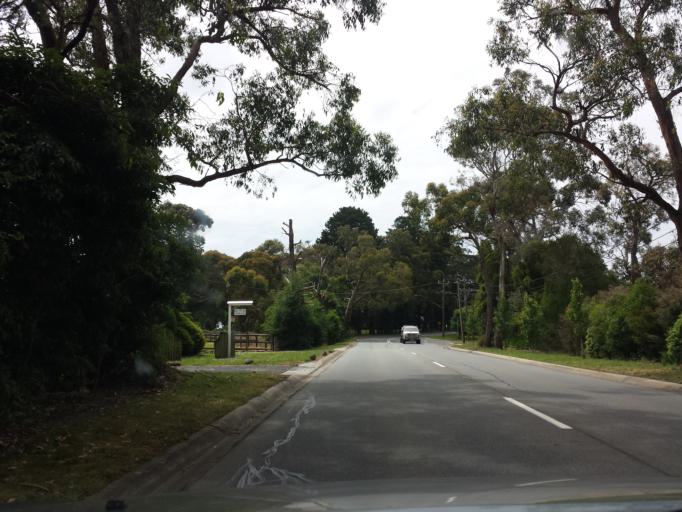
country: AU
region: Victoria
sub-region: Casey
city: Narre Warren North
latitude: -37.9970
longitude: 145.3456
